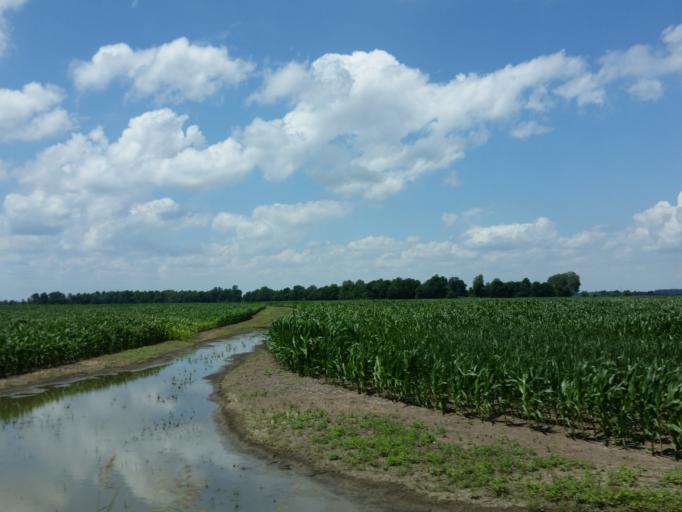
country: US
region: Kentucky
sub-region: Fulton County
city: Hickman
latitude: 36.5310
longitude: -89.3387
